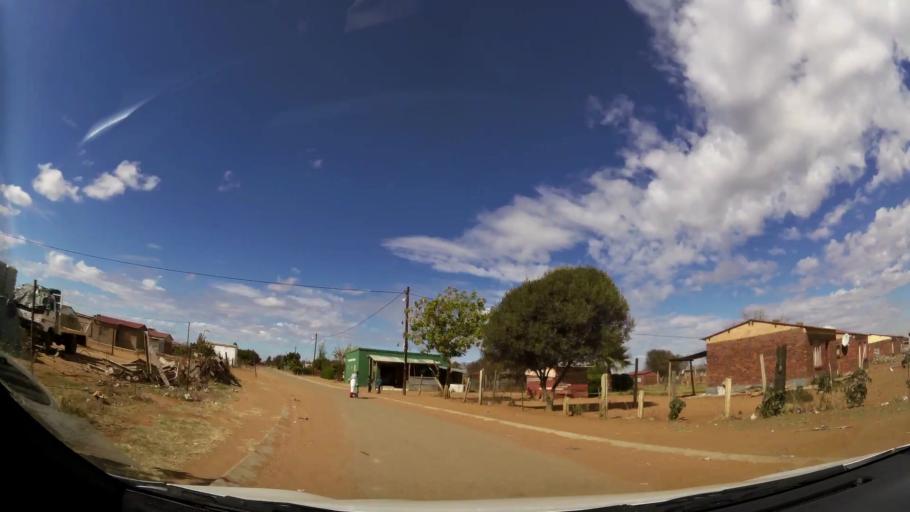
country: ZA
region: Limpopo
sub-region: Waterberg District Municipality
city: Bela-Bela
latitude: -24.8818
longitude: 28.3307
